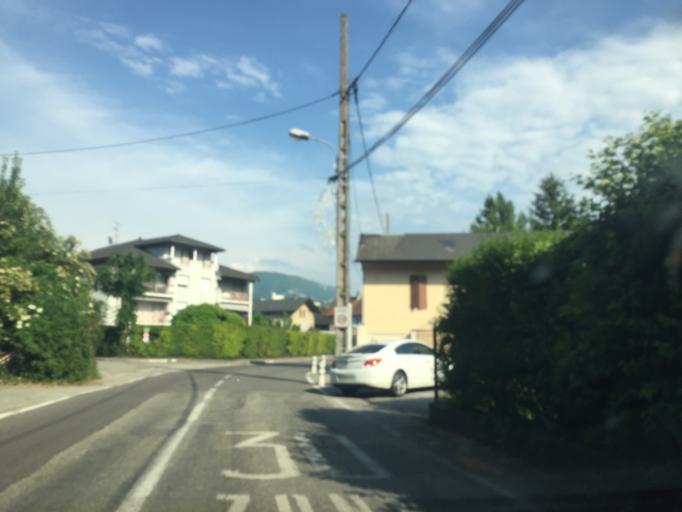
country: FR
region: Rhone-Alpes
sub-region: Departement de la Savoie
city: Chambery
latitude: 45.5741
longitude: 5.9376
